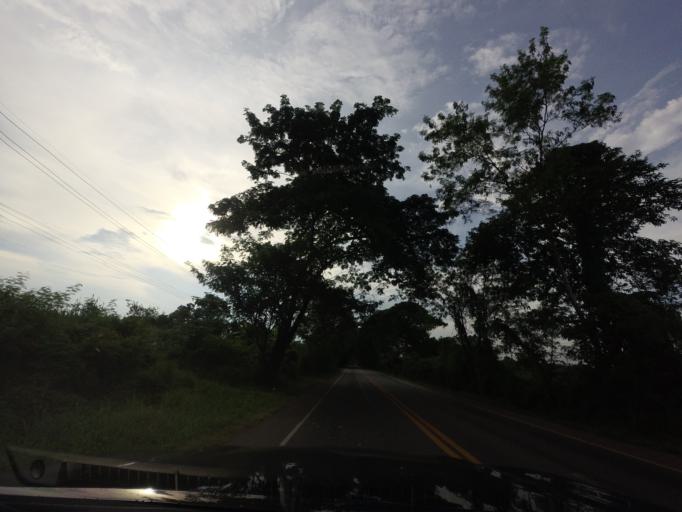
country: TH
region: Nong Khai
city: Pho Tak
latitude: 17.7835
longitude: 102.3753
